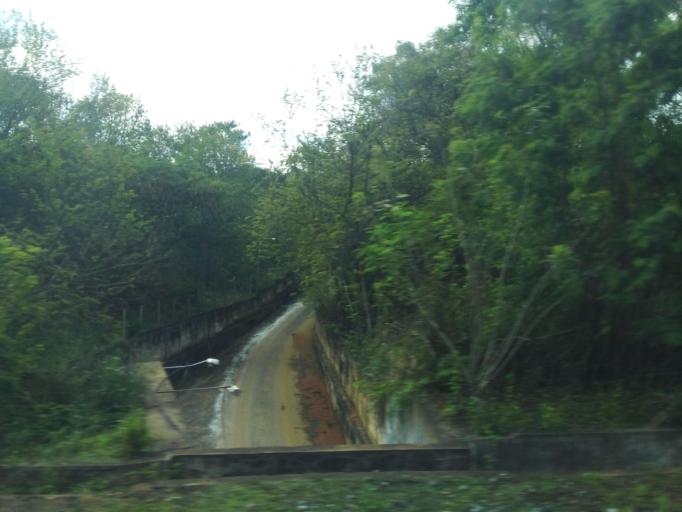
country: BR
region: Minas Gerais
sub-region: Governador Valadares
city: Governador Valadares
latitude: -18.9147
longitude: -42.0064
